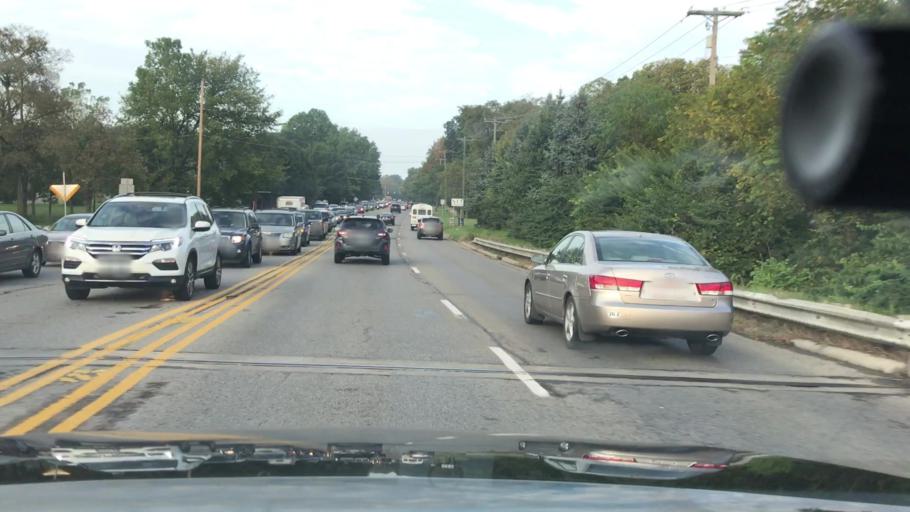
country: US
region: Ohio
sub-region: Franklin County
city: Upper Arlington
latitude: 40.0295
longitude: -83.0955
